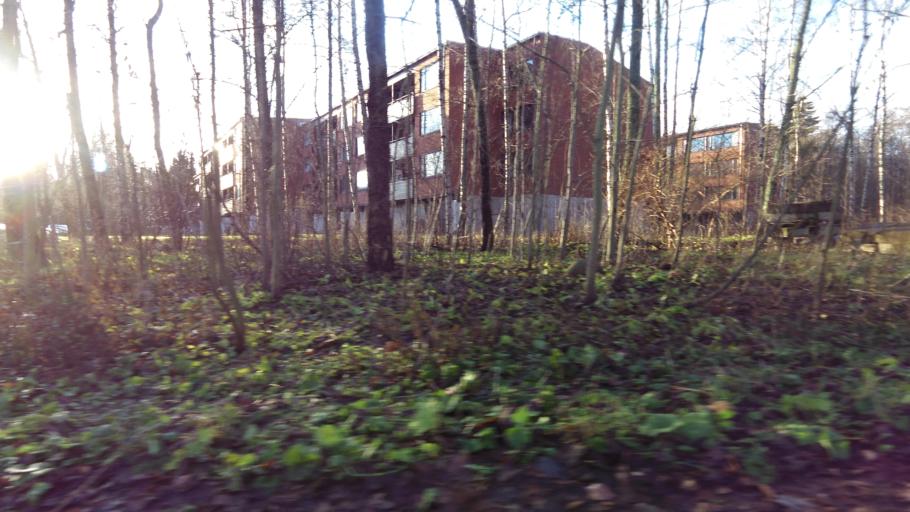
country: FI
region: Uusimaa
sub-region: Helsinki
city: Teekkarikylae
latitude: 60.1921
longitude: 24.8381
